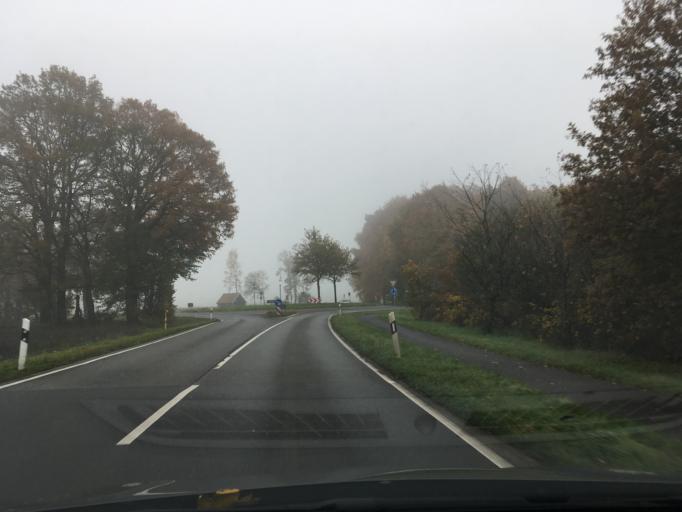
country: DE
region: North Rhine-Westphalia
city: Stadtlohn
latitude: 52.0633
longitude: 6.9328
